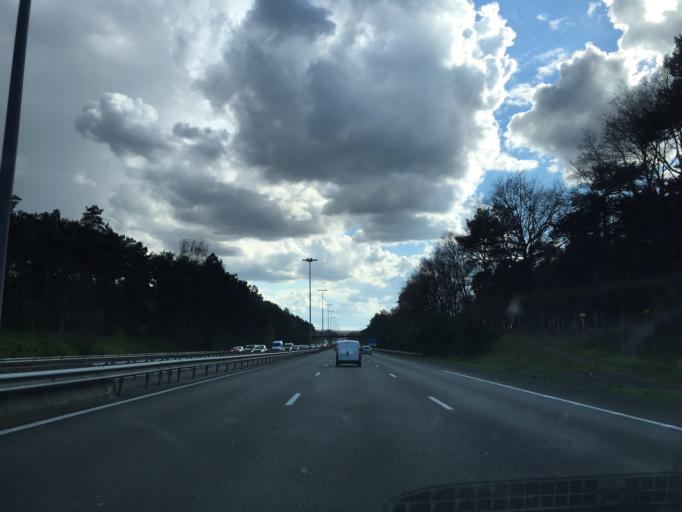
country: FR
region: Picardie
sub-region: Departement de l'Oise
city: Thiers-sur-Theve
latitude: 49.1590
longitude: 2.5941
